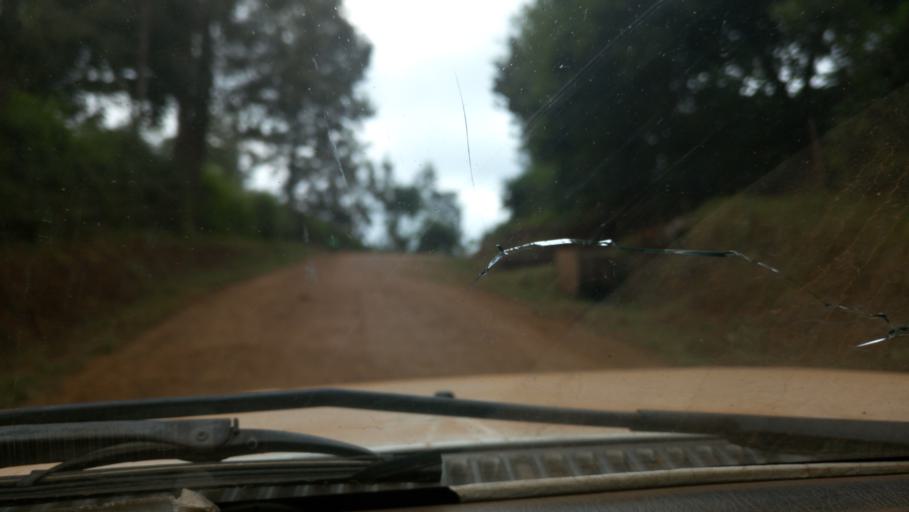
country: KE
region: Murang'a District
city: Kangema
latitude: -0.7176
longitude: 37.0367
